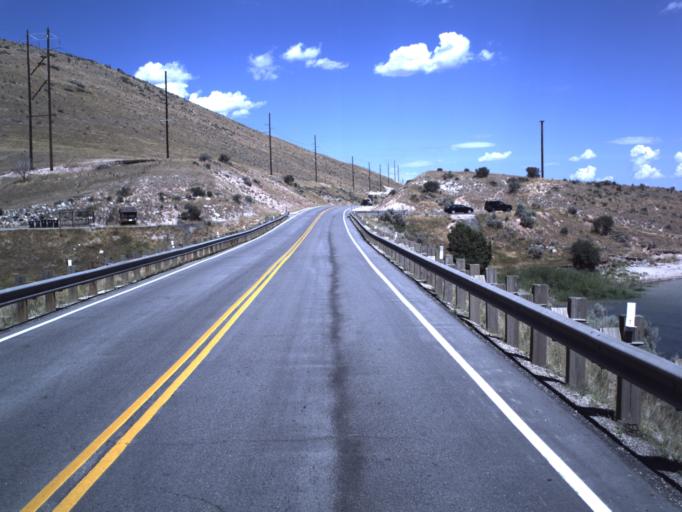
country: US
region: Utah
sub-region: Summit County
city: Oakley
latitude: 40.7756
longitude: -111.4083
